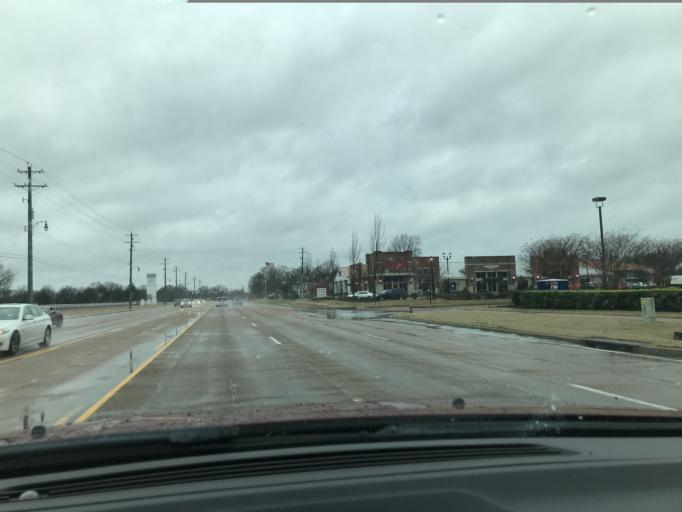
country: US
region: Tennessee
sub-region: Shelby County
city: Collierville
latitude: 35.0465
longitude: -89.7013
